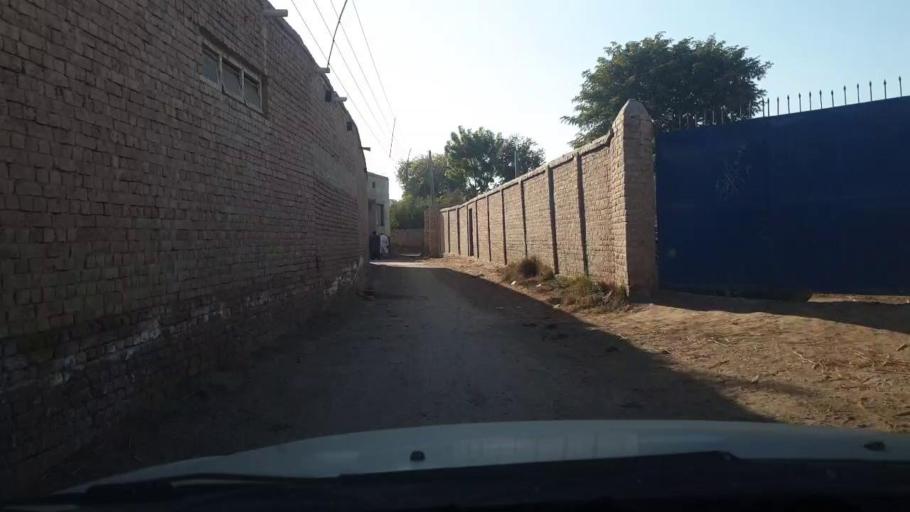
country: PK
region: Sindh
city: Ghotki
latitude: 28.0563
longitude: 69.3240
